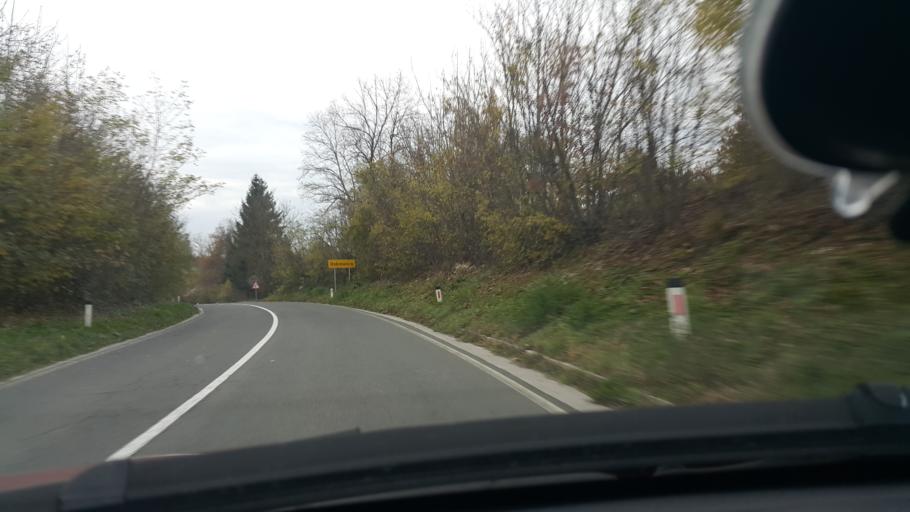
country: SI
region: Bistrica ob Sotli
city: Bistrica ob Sotli
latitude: 46.0760
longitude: 15.6387
